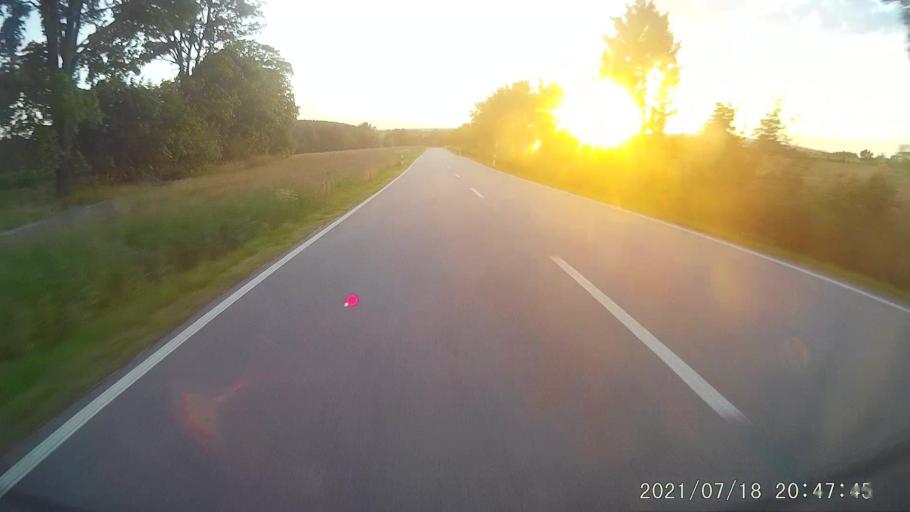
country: DE
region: Saxony
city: Reichenbach
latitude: 51.1860
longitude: 14.8030
